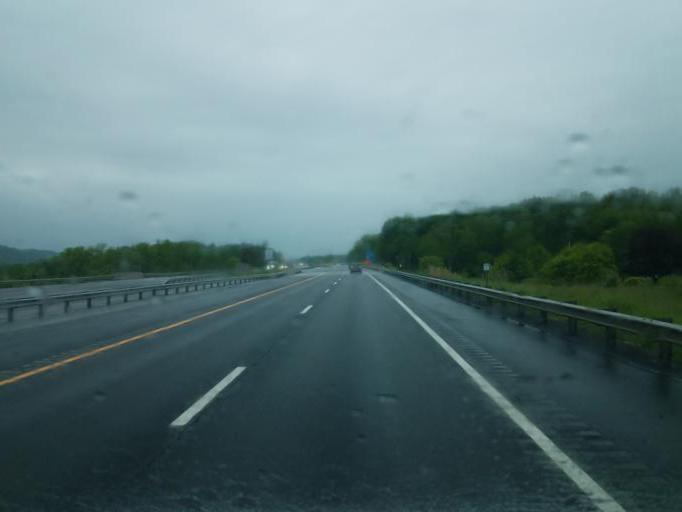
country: US
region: New York
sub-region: Herkimer County
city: Frankfort
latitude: 43.0549
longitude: -75.0665
